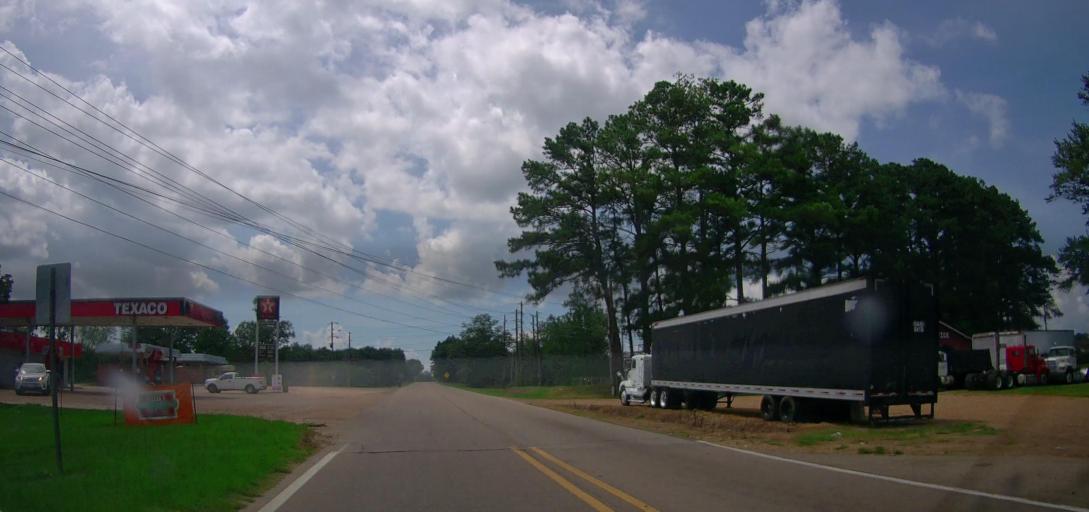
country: US
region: Mississippi
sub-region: Lee County
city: Shannon
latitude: 34.1193
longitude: -88.7073
